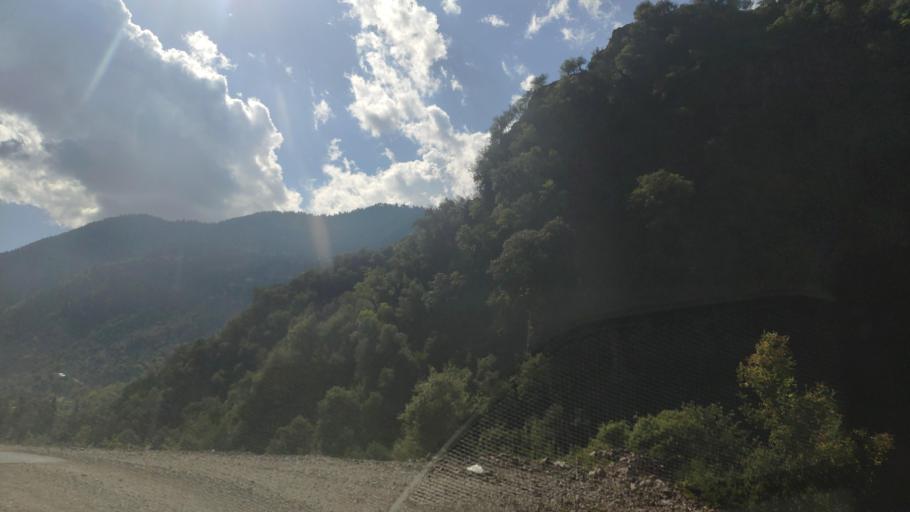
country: GR
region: Central Greece
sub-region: Nomos Evrytanias
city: Kerasochori
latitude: 39.1344
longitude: 21.6340
